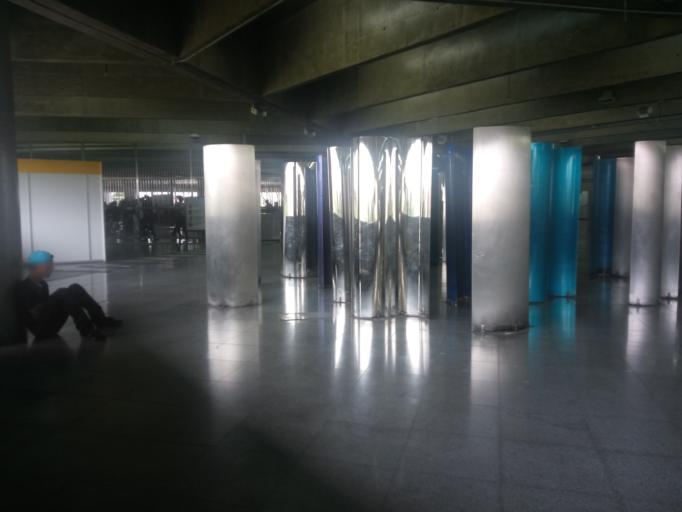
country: BR
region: Sao Paulo
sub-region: Sao Paulo
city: Sao Paulo
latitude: -23.5494
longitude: -46.6162
